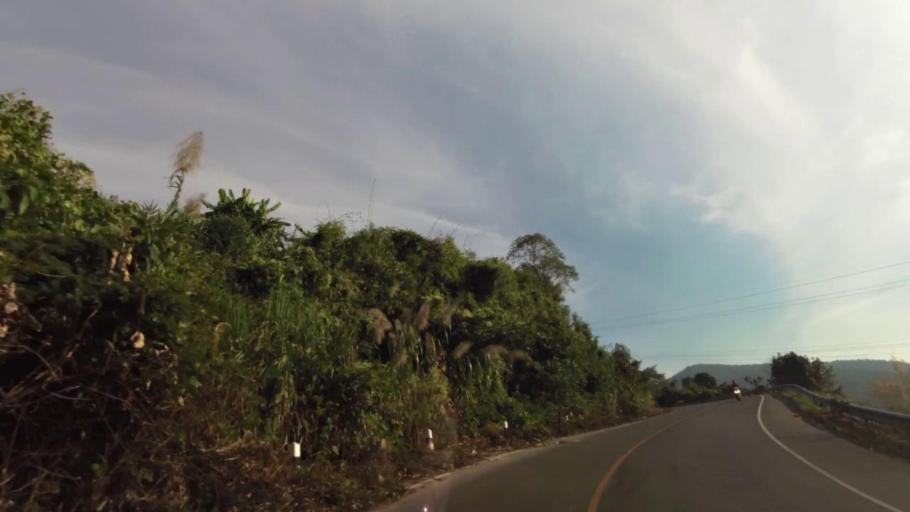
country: TH
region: Chiang Rai
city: Khun Tan
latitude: 19.8657
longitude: 100.4178
